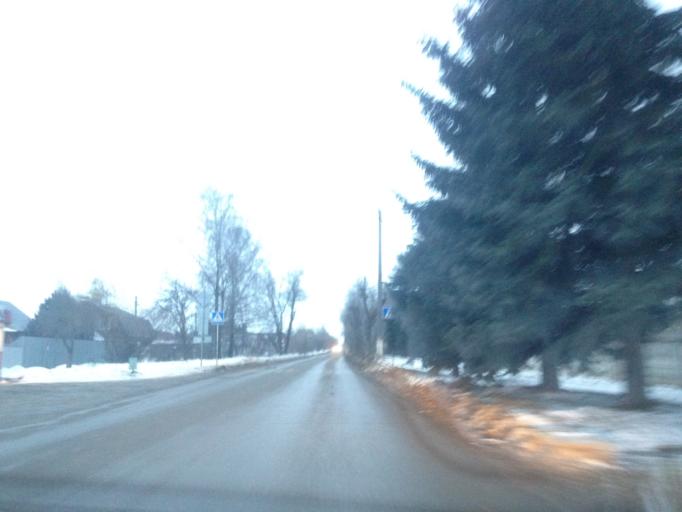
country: RU
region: Tula
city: Shchekino
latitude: 54.0042
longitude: 37.5270
